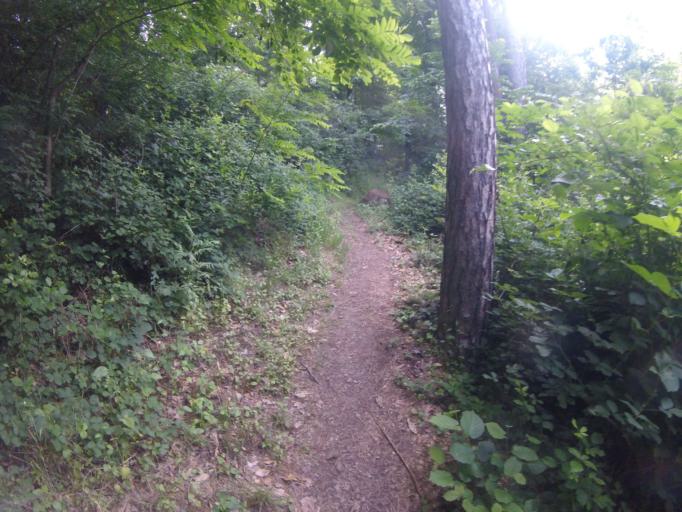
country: HU
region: Zala
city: Turje
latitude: 46.9083
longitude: 17.1720
